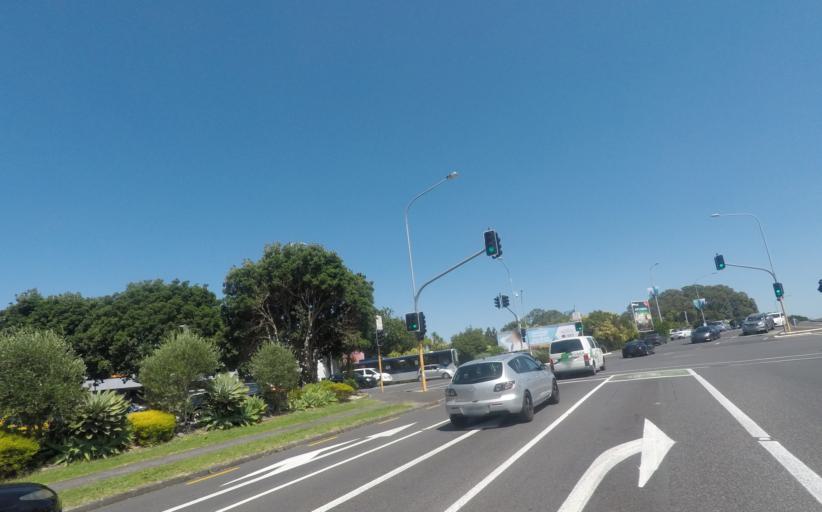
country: NZ
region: Auckland
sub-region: Auckland
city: Auckland
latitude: -36.8713
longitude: 174.7470
